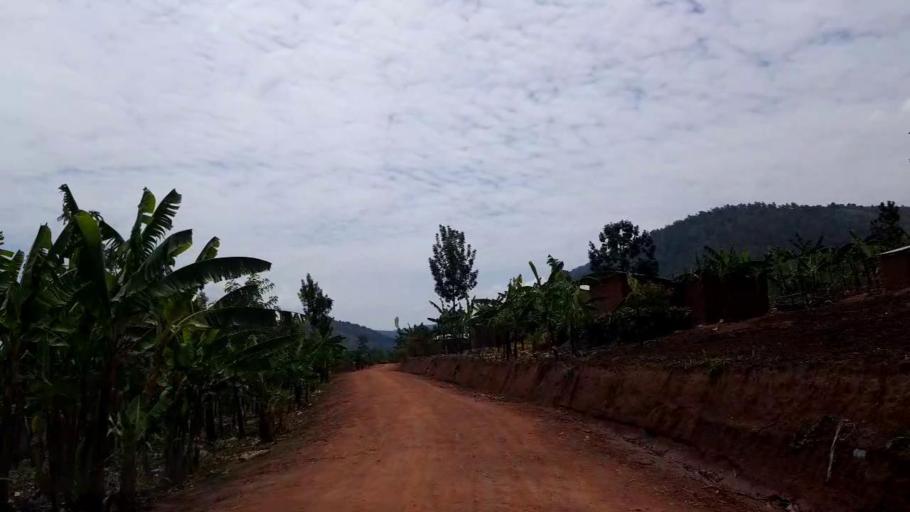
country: RW
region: Northern Province
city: Byumba
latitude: -1.5050
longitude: 30.1937
